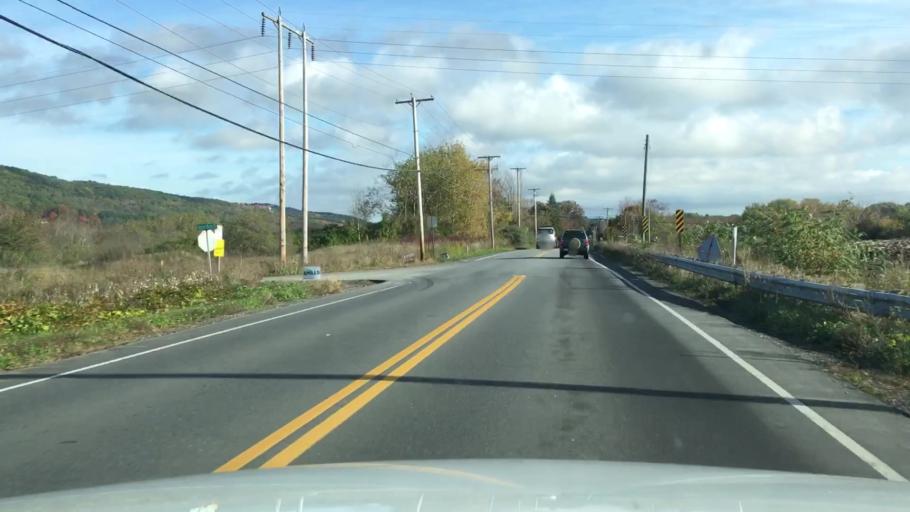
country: US
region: Maine
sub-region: Knox County
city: Rockland
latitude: 44.1088
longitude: -69.1355
